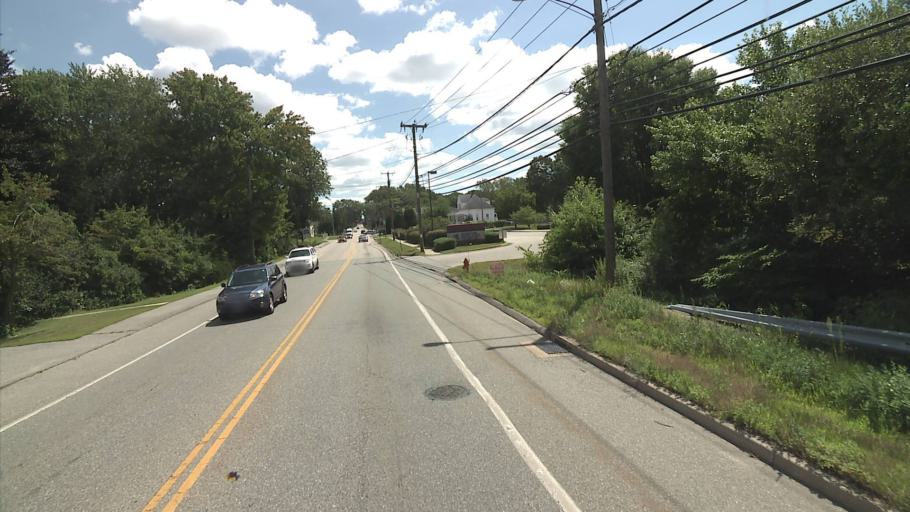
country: US
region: Connecticut
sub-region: New London County
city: Central Waterford
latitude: 41.3459
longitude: -72.1386
